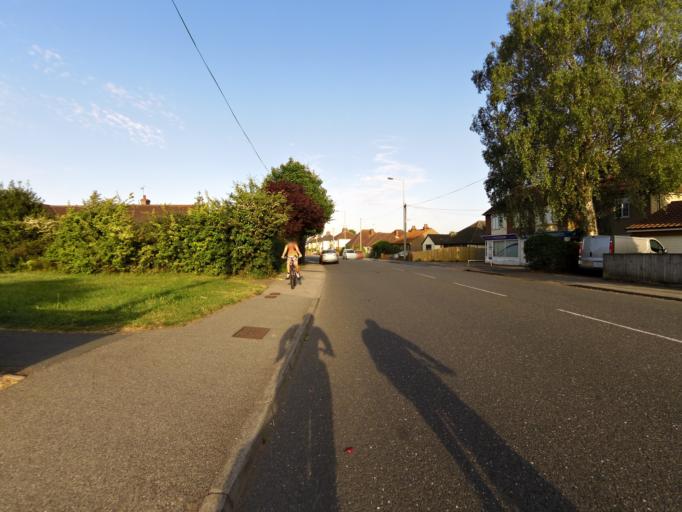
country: GB
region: England
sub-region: Suffolk
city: Kesgrave
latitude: 52.0496
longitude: 1.2068
